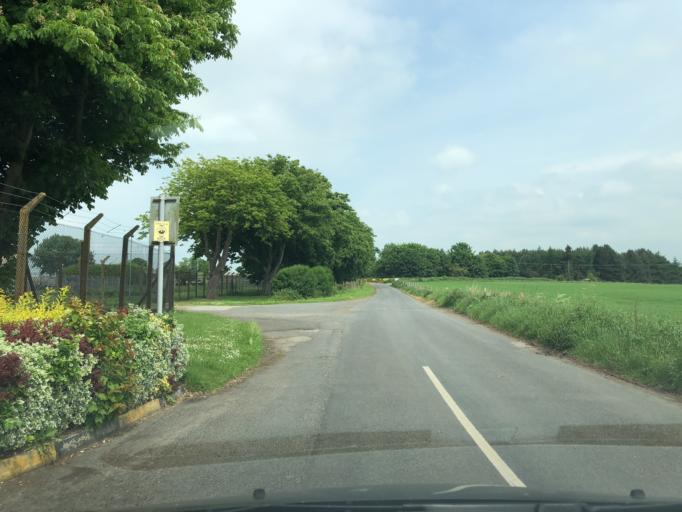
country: GB
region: England
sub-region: North Yorkshire
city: Boroughbridge
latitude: 54.1373
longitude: -1.4082
